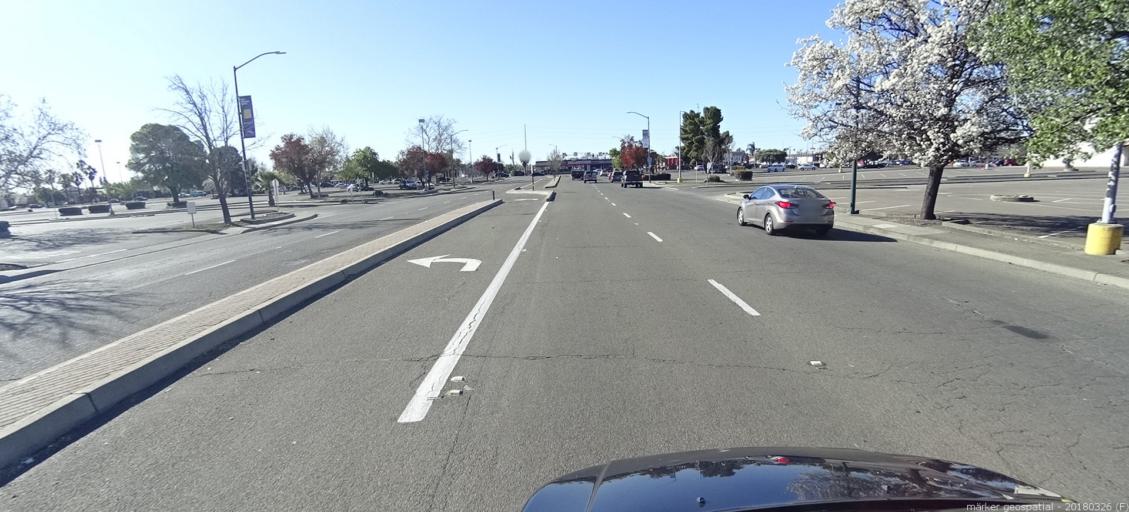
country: US
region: California
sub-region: Sacramento County
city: Parkway
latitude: 38.4980
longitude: -121.4381
